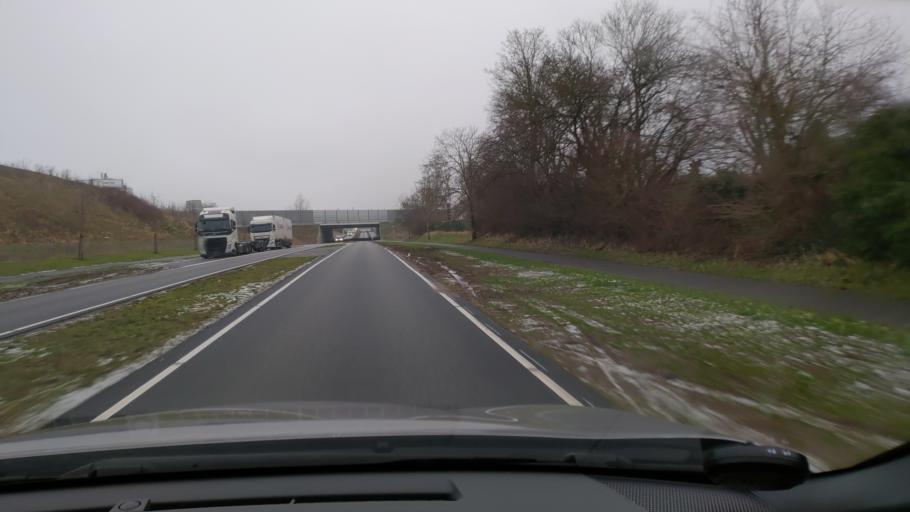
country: DK
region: Zealand
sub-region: Solrod Kommune
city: Solrod Strand
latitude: 55.5409
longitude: 12.2108
